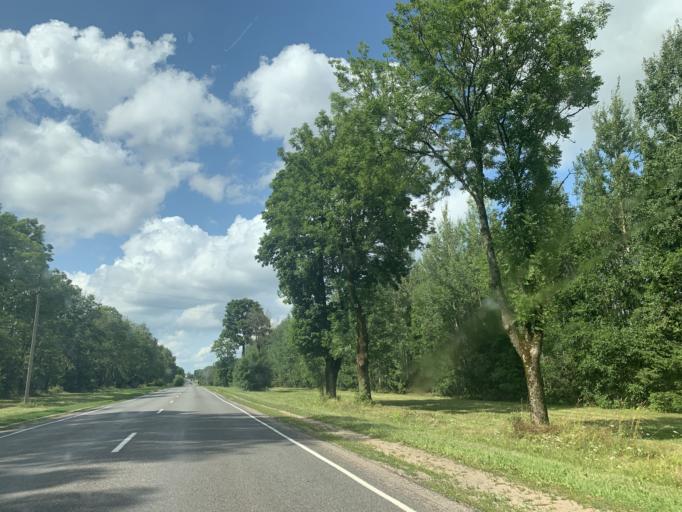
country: BY
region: Minsk
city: Enyerhyetykaw
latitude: 53.5747
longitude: 27.0602
